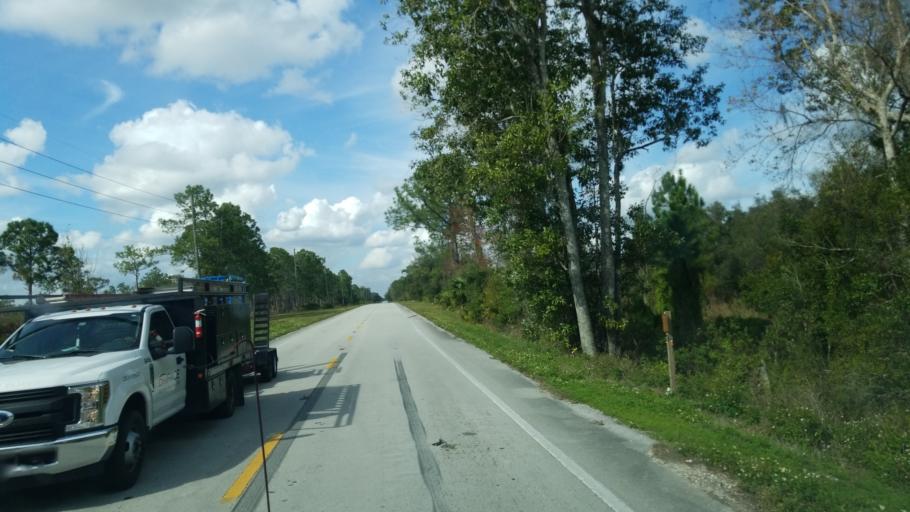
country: US
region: Florida
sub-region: Brevard County
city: June Park
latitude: 27.9704
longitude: -81.0078
